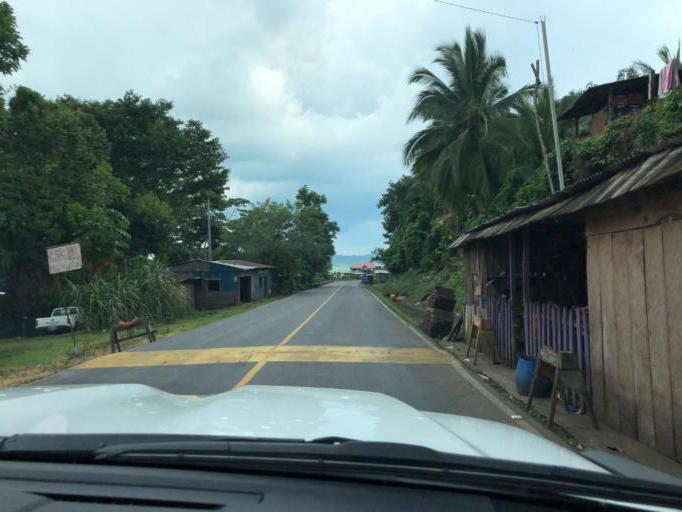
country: NI
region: Chontales
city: Villa Sandino
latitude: 11.9995
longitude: -84.7780
